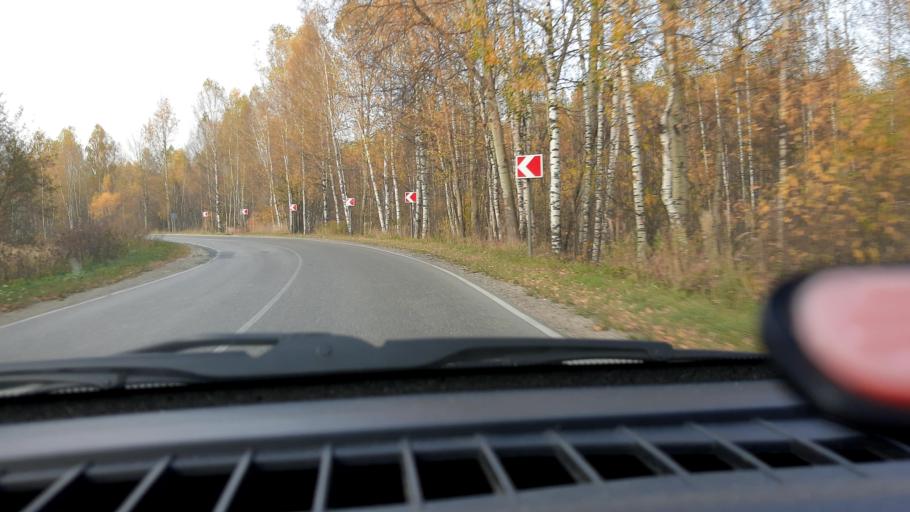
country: RU
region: Nizjnij Novgorod
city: Neklyudovo
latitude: 56.5018
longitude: 43.8504
